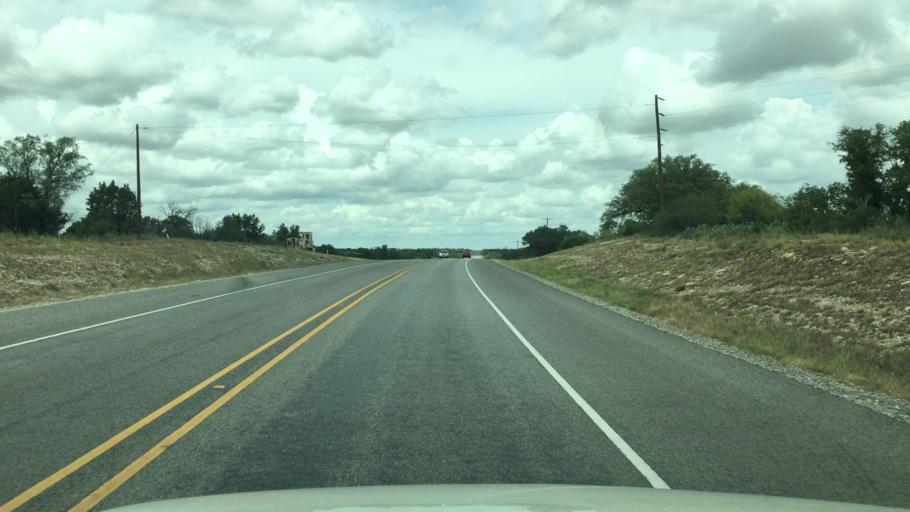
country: US
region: Texas
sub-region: McCulloch County
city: Brady
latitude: 31.0339
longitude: -99.2345
